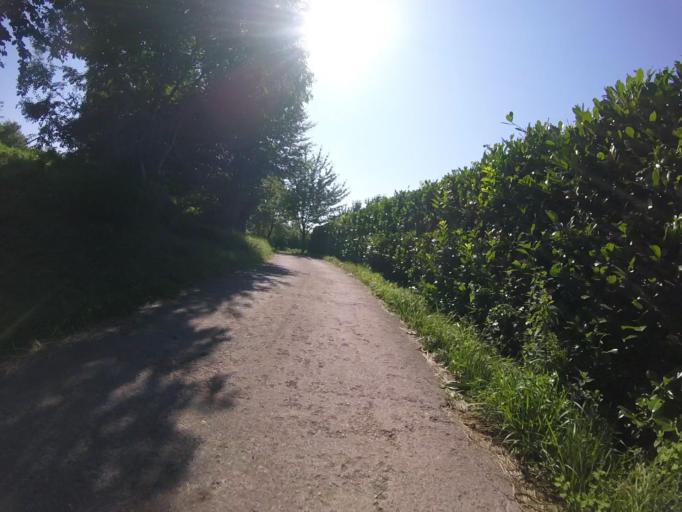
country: ES
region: Basque Country
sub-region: Provincia de Guipuzcoa
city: Astigarraga
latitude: 43.2786
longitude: -1.9352
